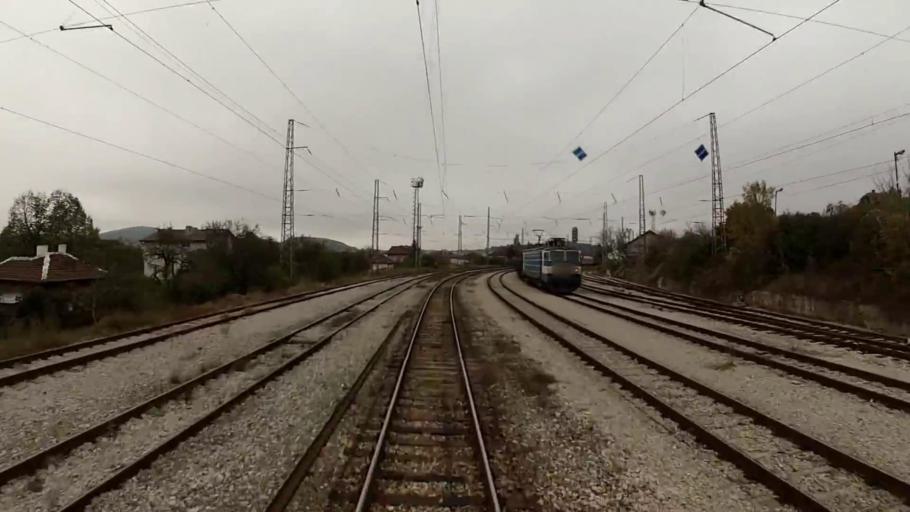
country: BG
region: Sofiya
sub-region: Obshtina Dragoman
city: Dragoman
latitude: 42.9294
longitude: 22.9309
